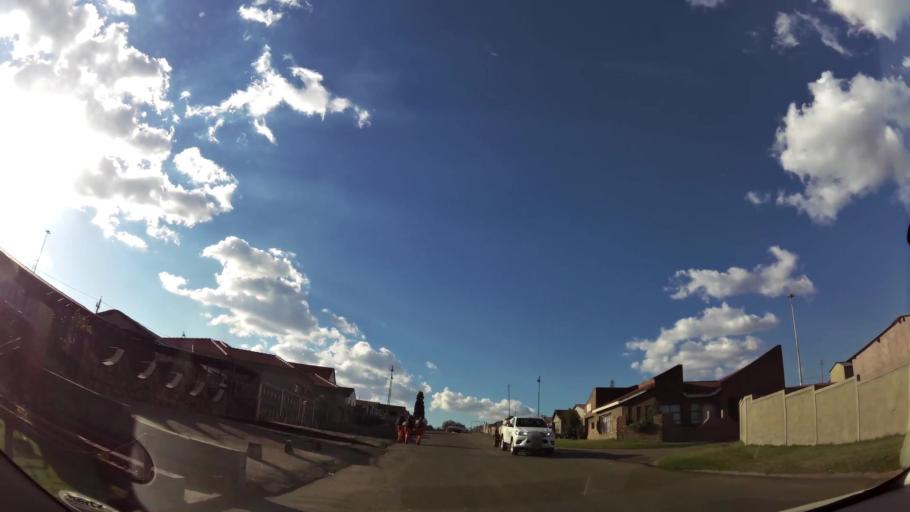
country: ZA
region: Mpumalanga
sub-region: Nkangala District Municipality
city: Witbank
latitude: -25.8730
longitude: 29.1891
